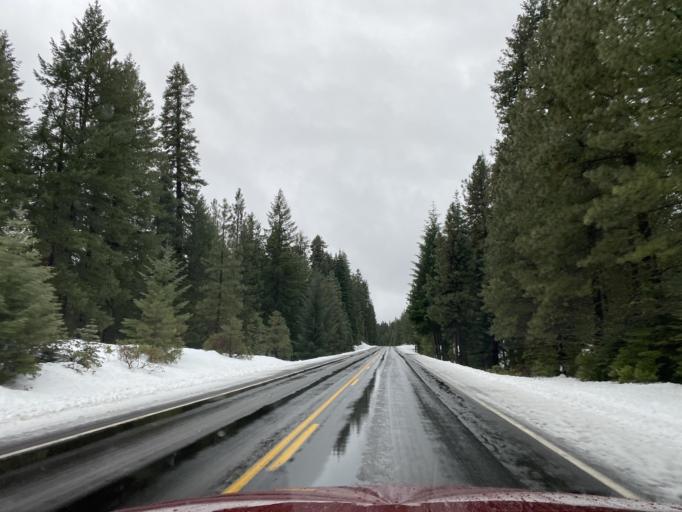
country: US
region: Oregon
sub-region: Klamath County
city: Klamath Falls
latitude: 42.5022
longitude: -122.0831
